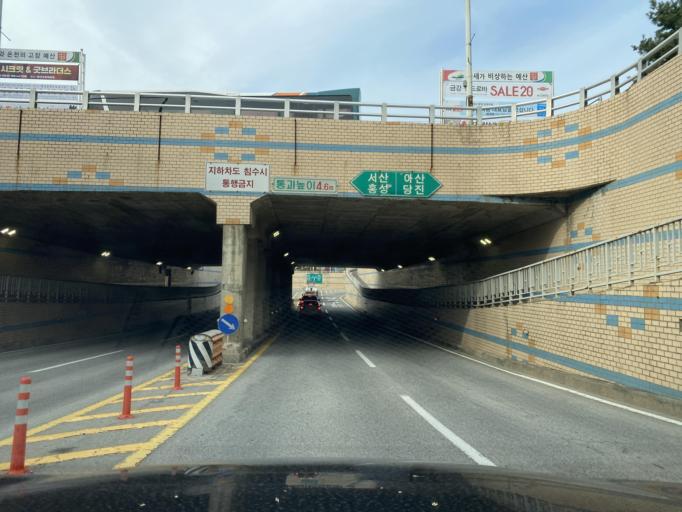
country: KR
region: Chungcheongnam-do
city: Yesan
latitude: 36.6939
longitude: 126.8297
